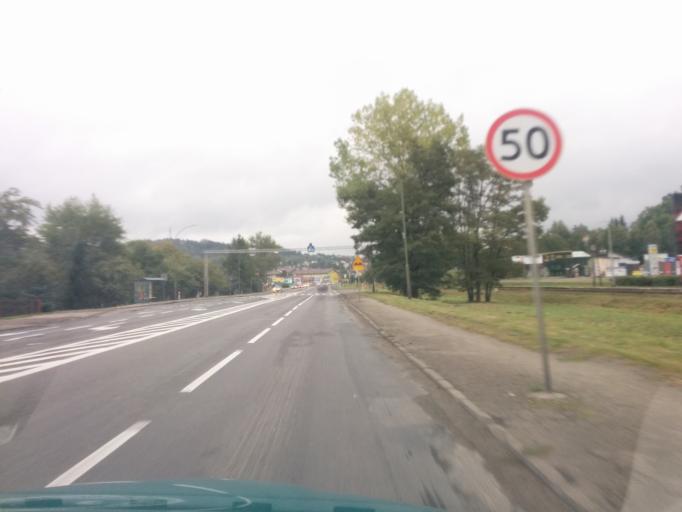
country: PL
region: Subcarpathian Voivodeship
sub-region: Powiat sanocki
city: Sanok
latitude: 49.5694
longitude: 22.1590
